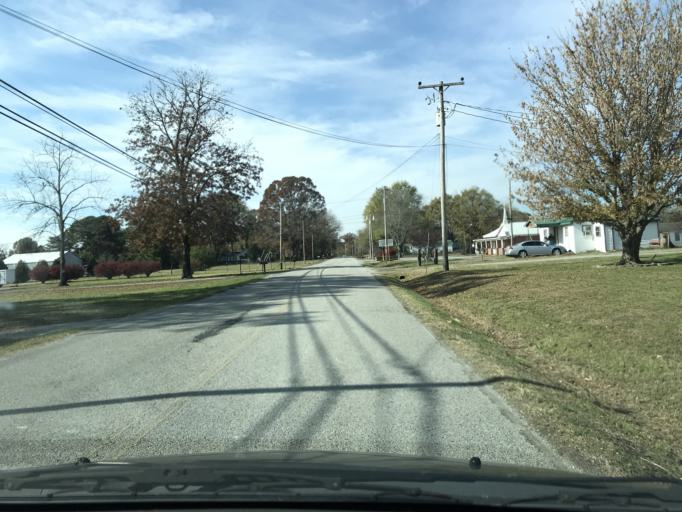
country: US
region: Tennessee
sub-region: Coffee County
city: Tullahoma
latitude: 35.3900
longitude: -86.1586
